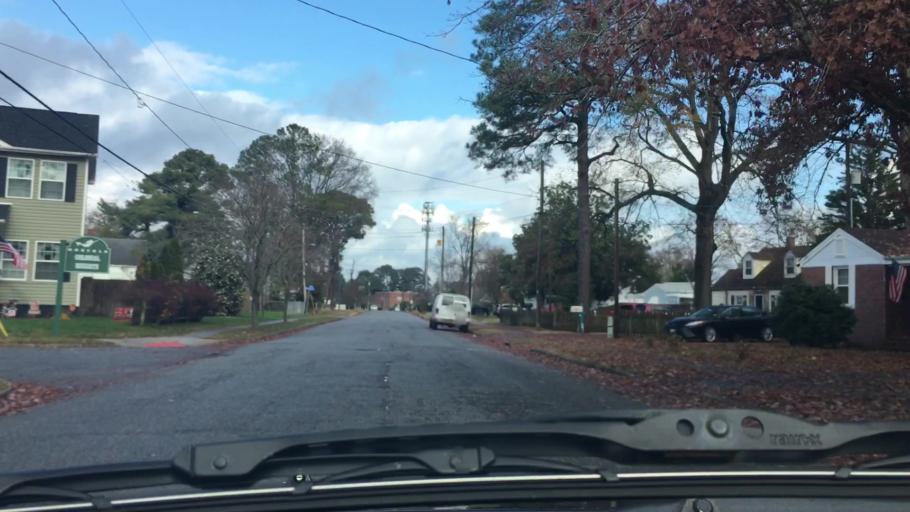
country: US
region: Virginia
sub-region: City of Norfolk
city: Norfolk
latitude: 36.9259
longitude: -76.2457
